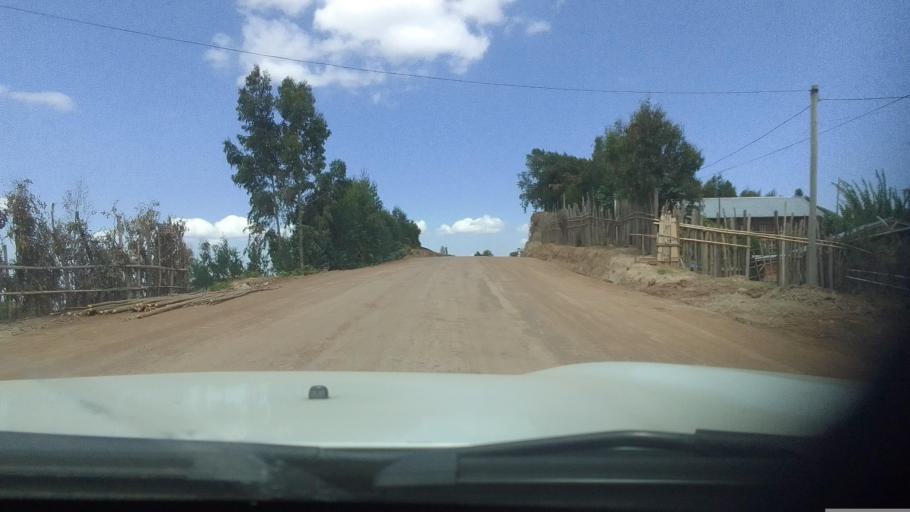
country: ET
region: Oromiya
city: Hagere Hiywet
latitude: 8.8410
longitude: 37.8854
